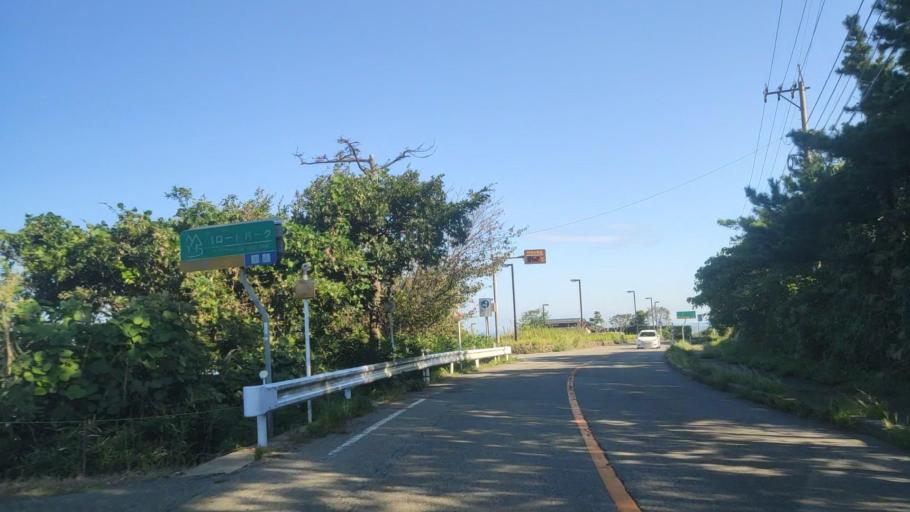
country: JP
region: Ishikawa
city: Hakui
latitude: 36.9322
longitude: 136.7562
